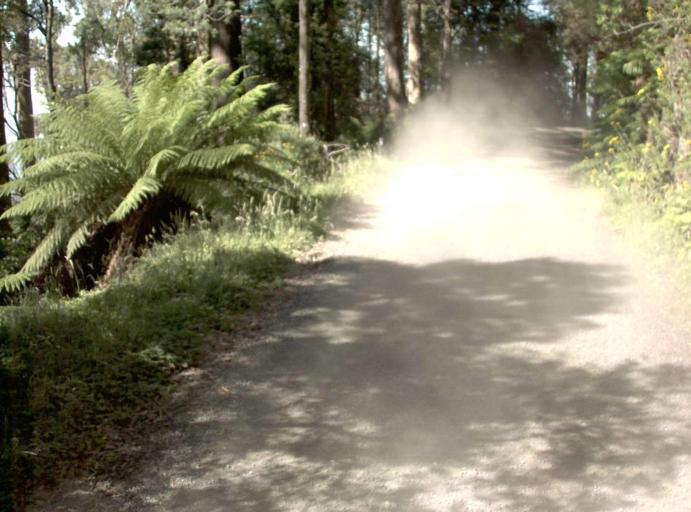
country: AU
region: Victoria
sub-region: Yarra Ranges
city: Millgrove
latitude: -37.7148
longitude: 145.6342
